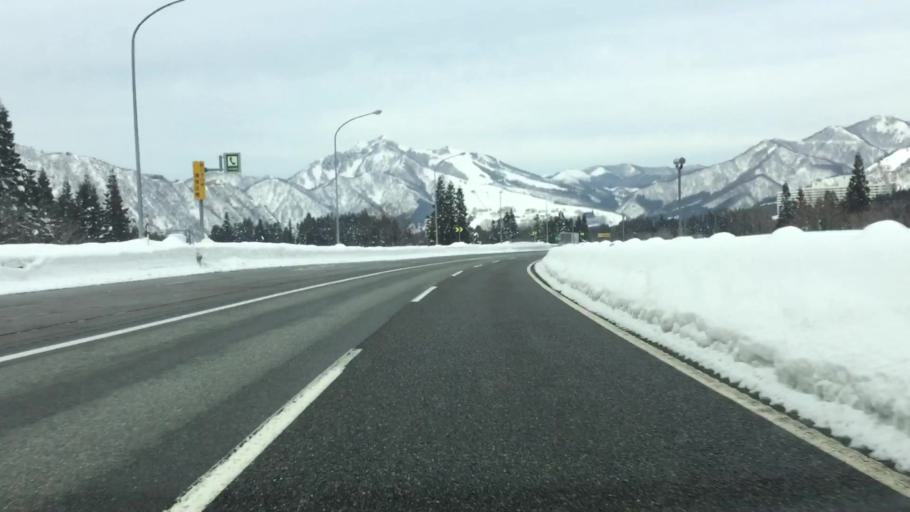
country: JP
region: Niigata
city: Shiozawa
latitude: 36.8953
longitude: 138.8452
